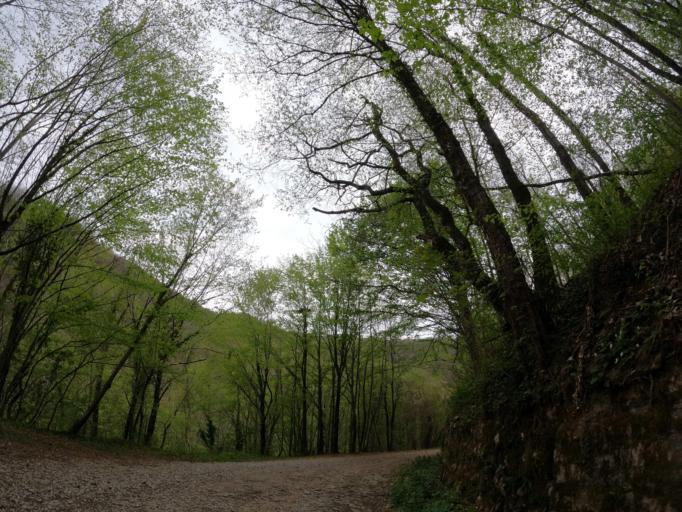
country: IT
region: Friuli Venezia Giulia
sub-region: Provincia di Udine
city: Stregna
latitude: 46.1184
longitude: 13.6119
